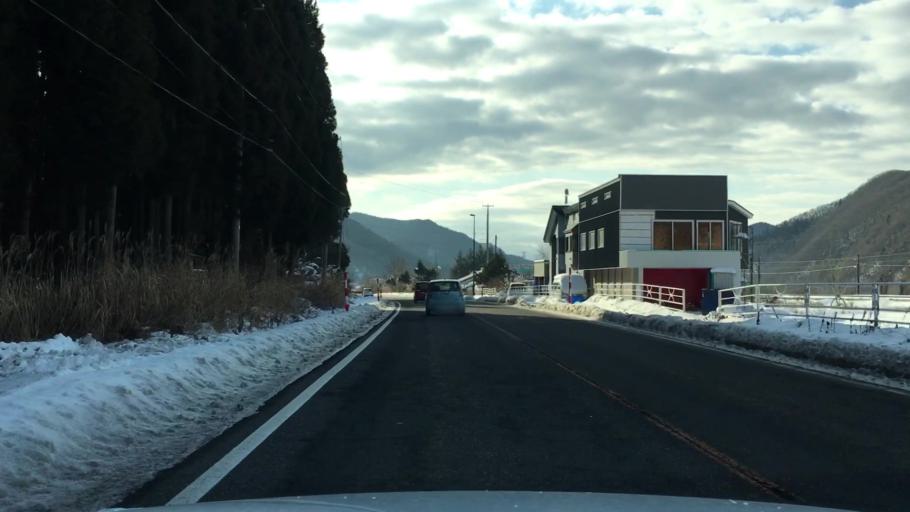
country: JP
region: Akita
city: Odate
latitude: 40.3580
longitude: 140.5979
